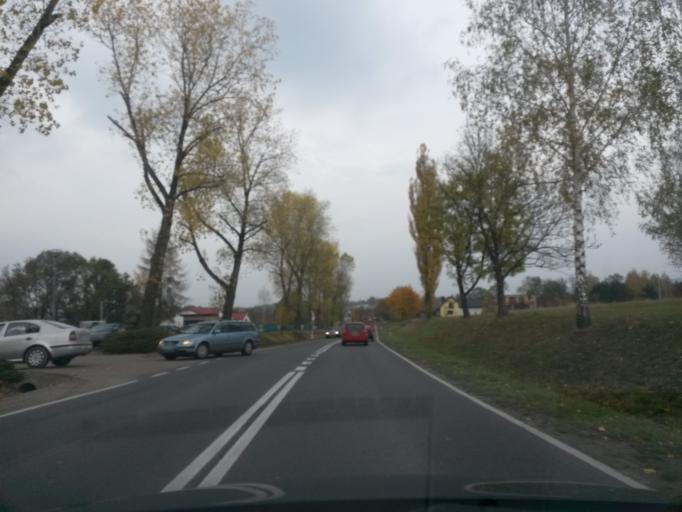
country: PL
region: Lower Silesian Voivodeship
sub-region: Powiat klodzki
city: Klodzko
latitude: 50.4150
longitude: 16.6595
